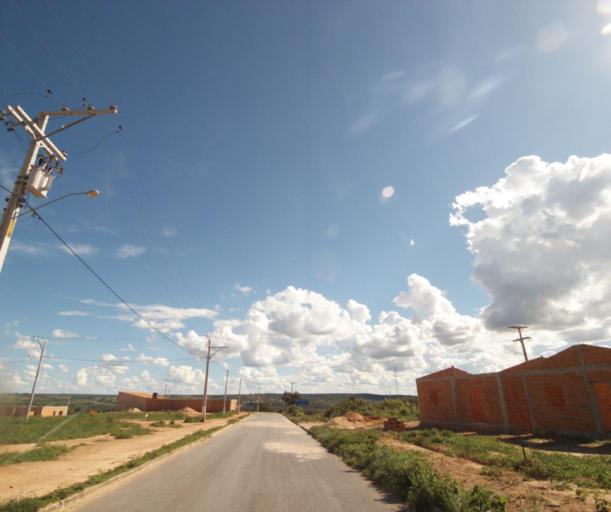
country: BR
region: Bahia
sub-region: Correntina
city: Correntina
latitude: -13.3287
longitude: -44.6378
